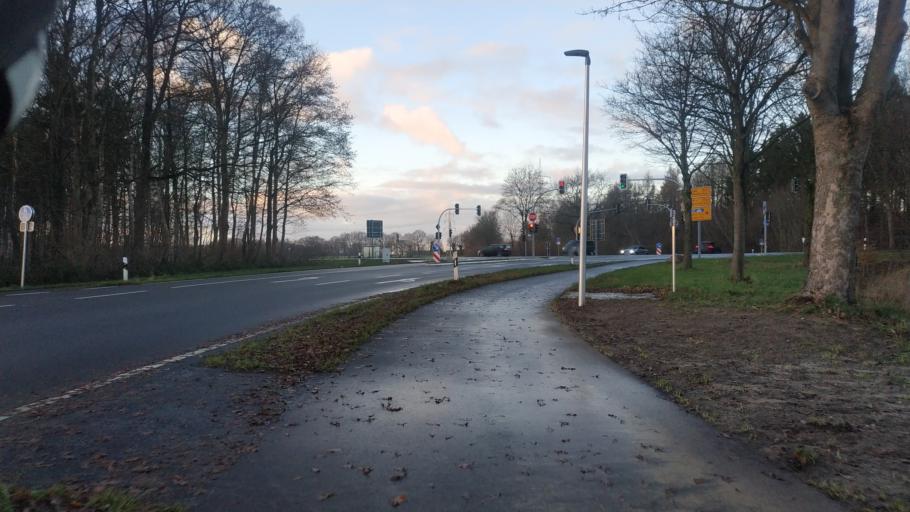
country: DE
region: North Rhine-Westphalia
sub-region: Regierungsbezirk Munster
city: Mettingen
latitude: 52.2821
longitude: 7.7820
